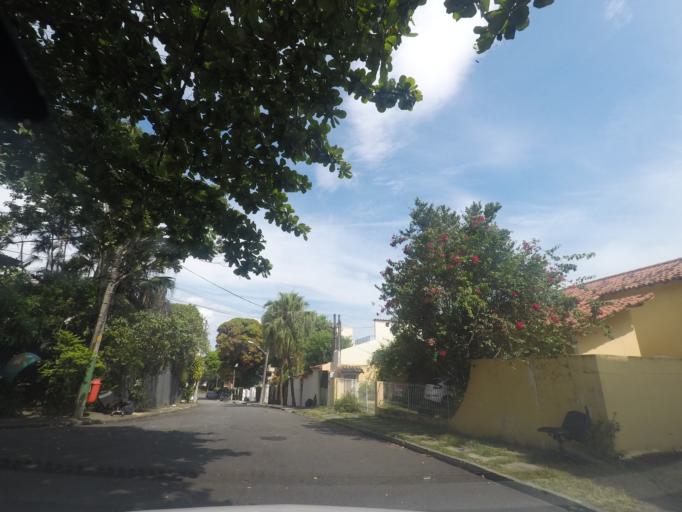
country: BR
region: Rio de Janeiro
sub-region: Rio De Janeiro
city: Rio de Janeiro
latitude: -22.8185
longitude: -43.1929
